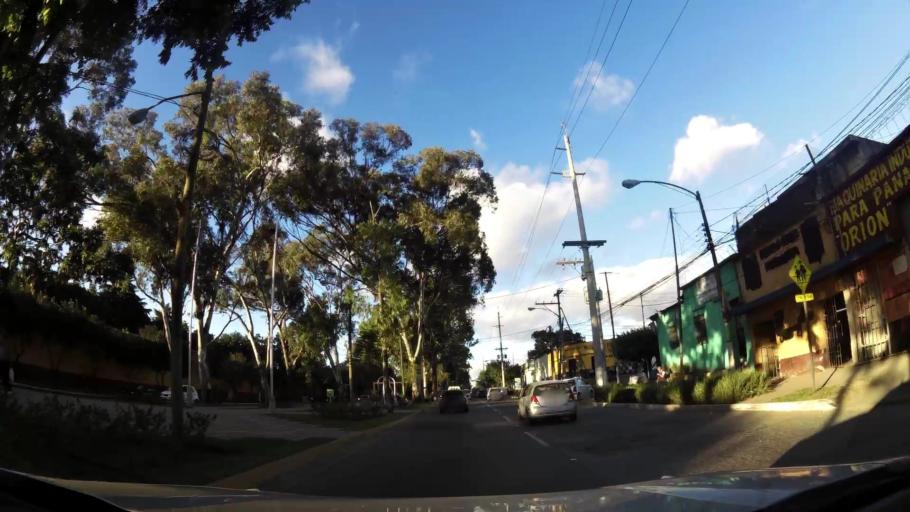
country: GT
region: Guatemala
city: Guatemala City
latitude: 14.6260
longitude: -90.5274
